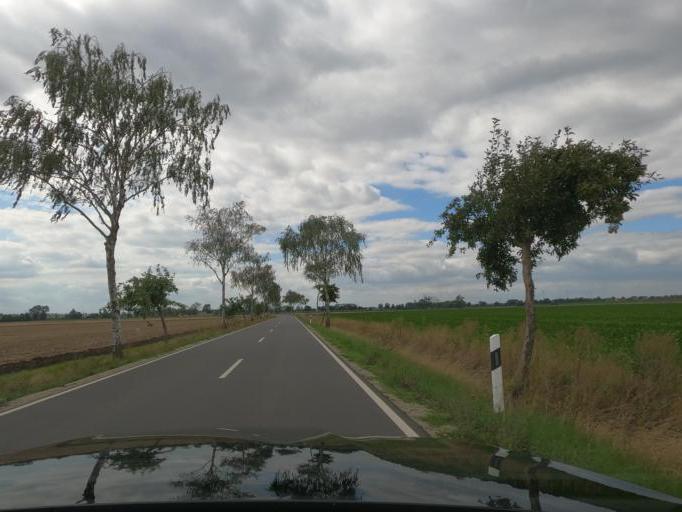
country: DE
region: Lower Saxony
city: Hohenhameln
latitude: 52.2270
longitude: 10.0786
